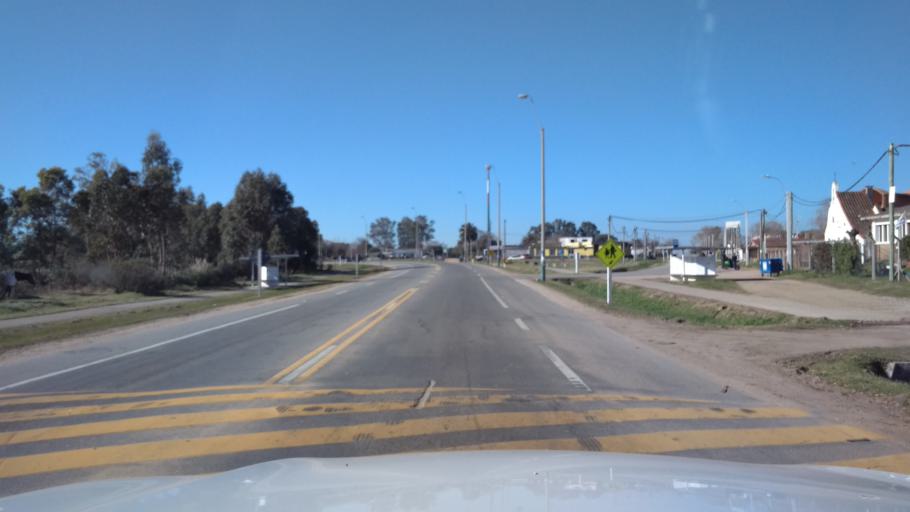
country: UY
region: Canelones
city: Atlantida
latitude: -34.7439
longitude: -55.7675
